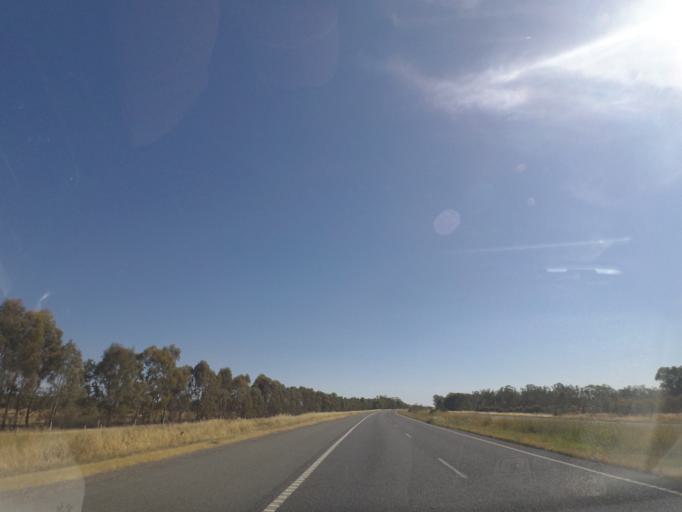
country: AU
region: Victoria
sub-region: Greater Shepparton
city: Shepparton
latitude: -36.6589
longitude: 145.2815
